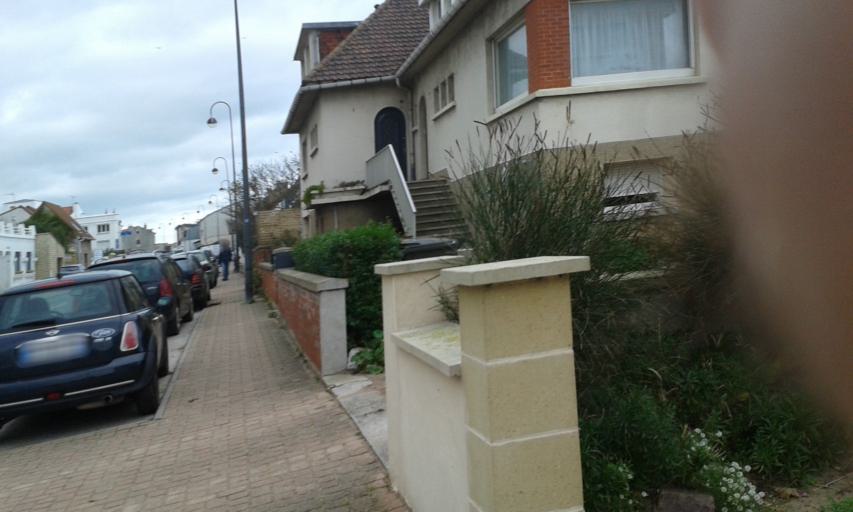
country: FR
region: Nord-Pas-de-Calais
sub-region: Departement du Pas-de-Calais
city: Sangatte
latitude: 50.9441
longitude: 1.7460
